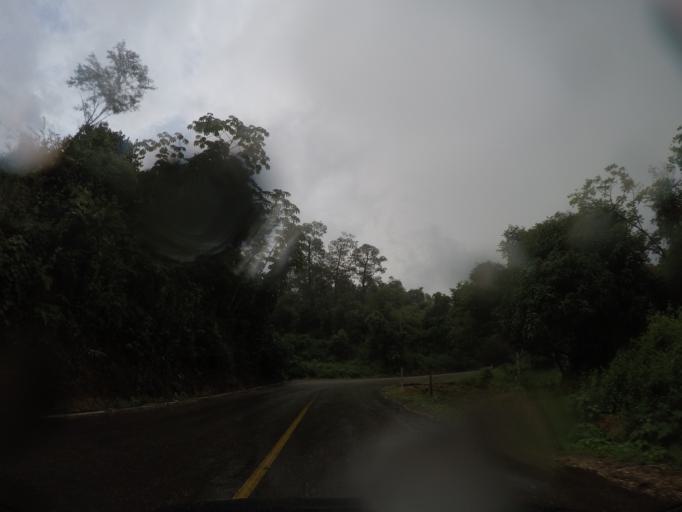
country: MX
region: Oaxaca
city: San Gabriel Mixtepec
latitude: 16.0838
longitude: -97.0803
